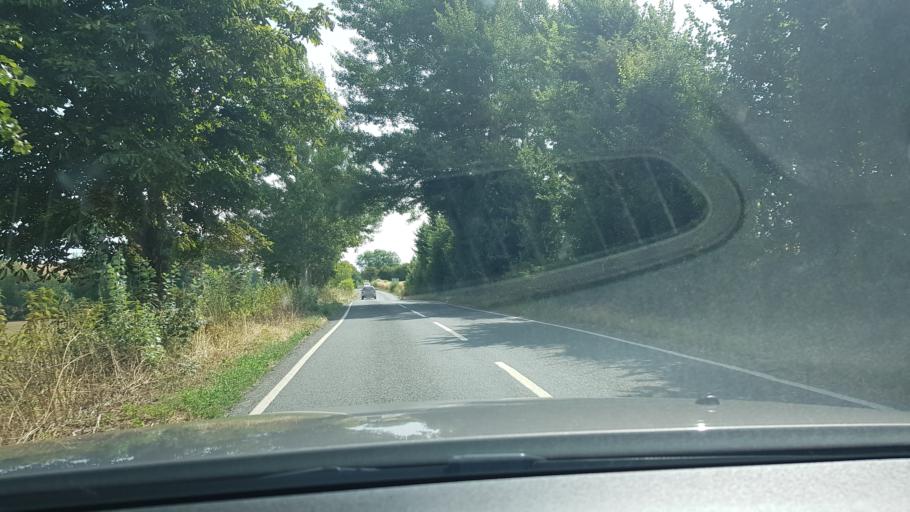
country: GB
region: England
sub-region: West Berkshire
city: Wickham
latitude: 51.4791
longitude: -1.4646
